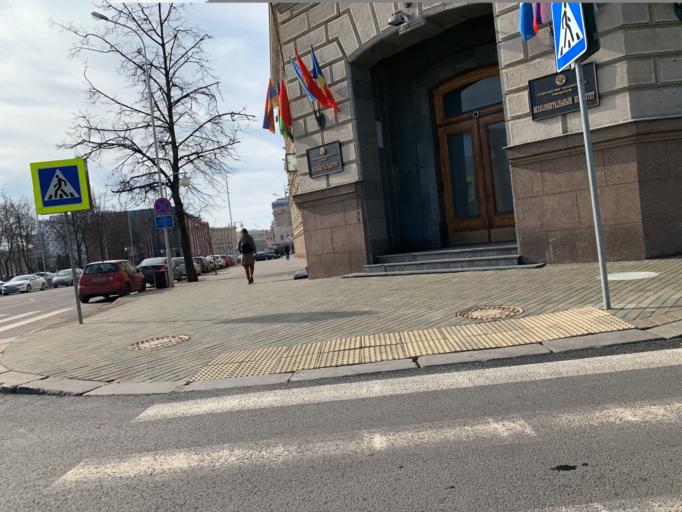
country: BY
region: Minsk
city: Minsk
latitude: 53.8966
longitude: 27.5579
